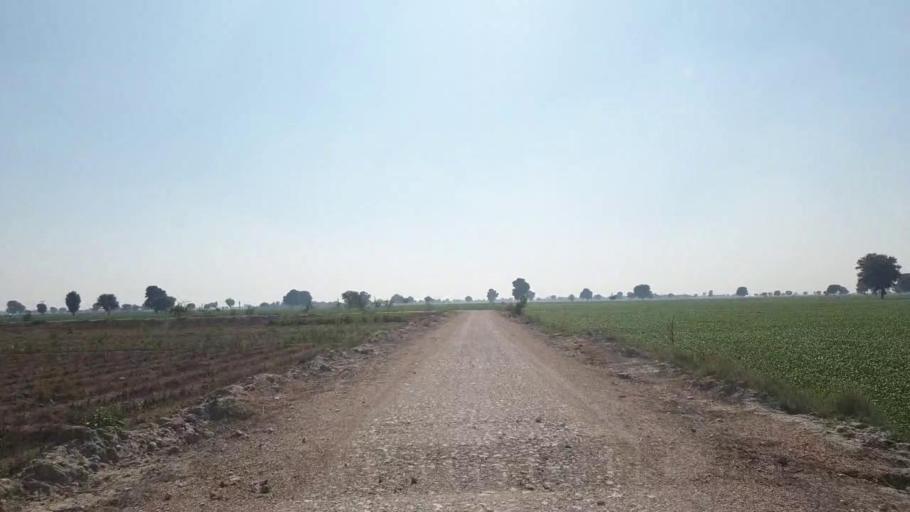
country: PK
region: Sindh
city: Shahpur Chakar
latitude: 26.1047
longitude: 68.6308
